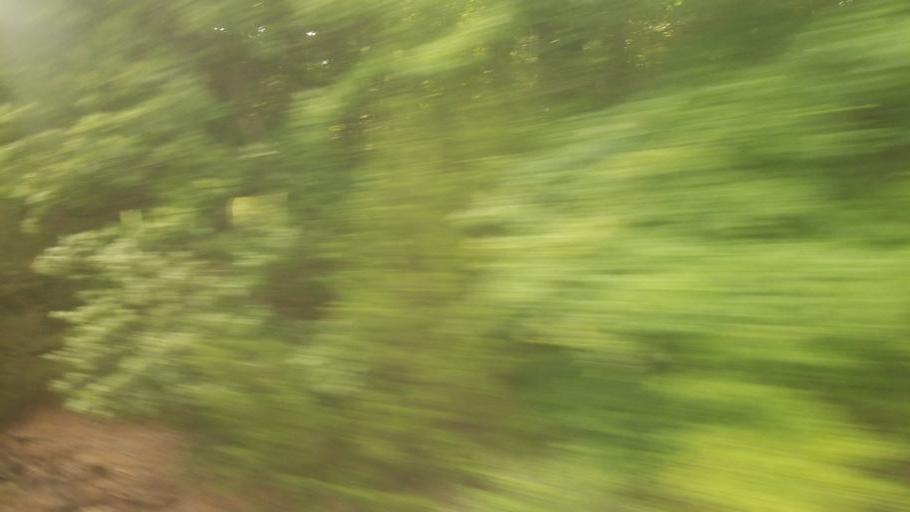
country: US
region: Kansas
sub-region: Wyandotte County
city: Bonner Springs
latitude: 38.9991
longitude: -94.8998
